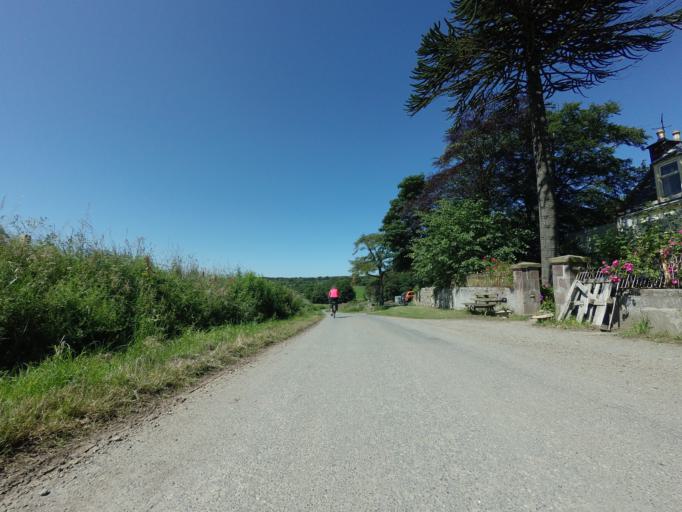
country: GB
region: Scotland
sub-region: Aberdeenshire
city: Macduff
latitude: 57.6419
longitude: -2.5040
